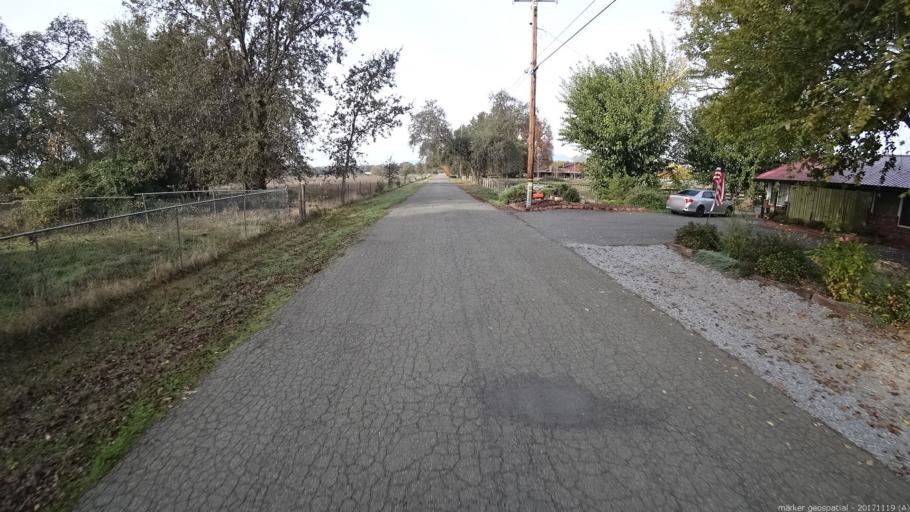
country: US
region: California
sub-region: Shasta County
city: Anderson
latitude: 40.5020
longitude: -122.3284
